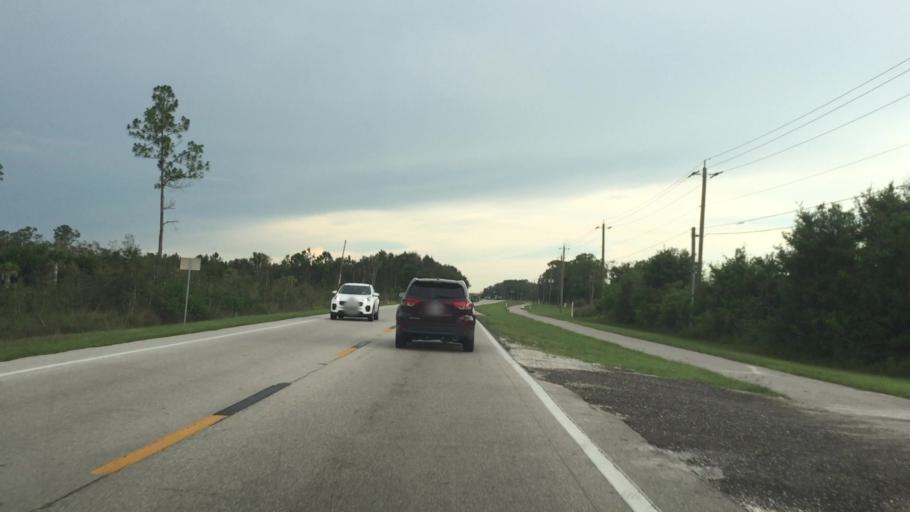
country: US
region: Florida
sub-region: Lee County
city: Fort Myers
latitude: 26.6294
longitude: -81.8115
